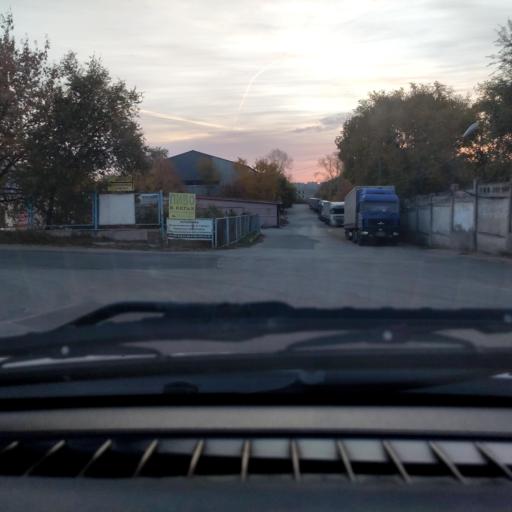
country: RU
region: Samara
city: Zhigulevsk
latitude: 53.4818
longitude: 49.4915
